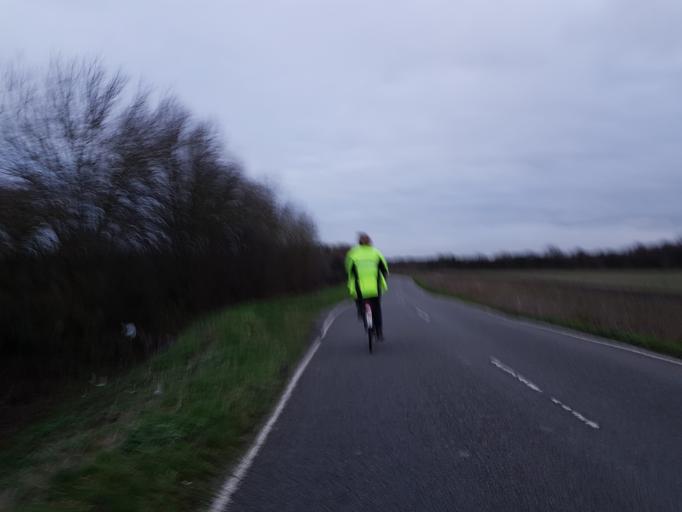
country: GB
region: England
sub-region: Cambridgeshire
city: Fulbourn
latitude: 52.2152
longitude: 0.1940
